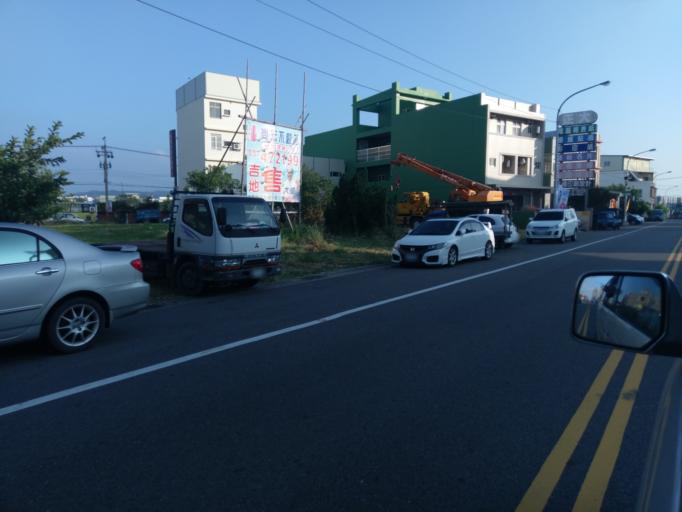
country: TW
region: Taiwan
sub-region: Miaoli
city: Miaoli
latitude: 24.6808
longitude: 120.8781
